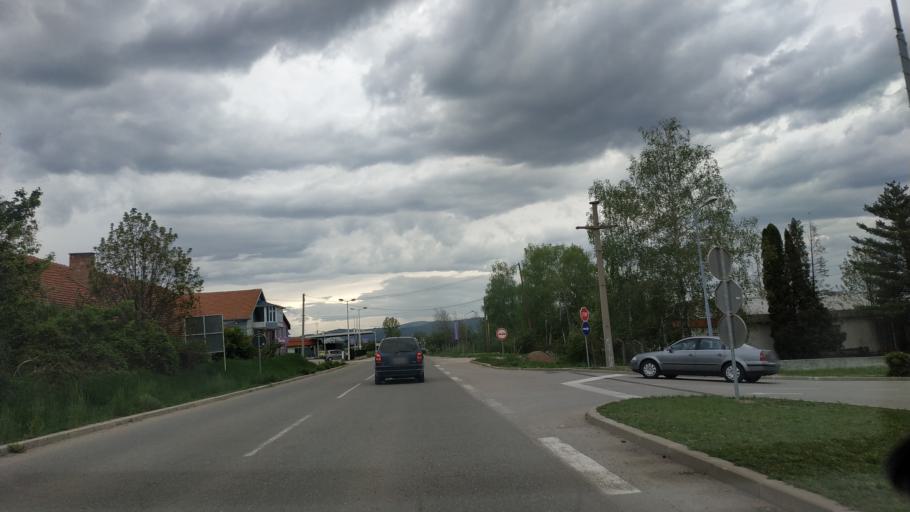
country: RS
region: Central Serbia
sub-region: Zajecarski Okrug
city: Soko Banja
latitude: 43.6521
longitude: 21.8478
